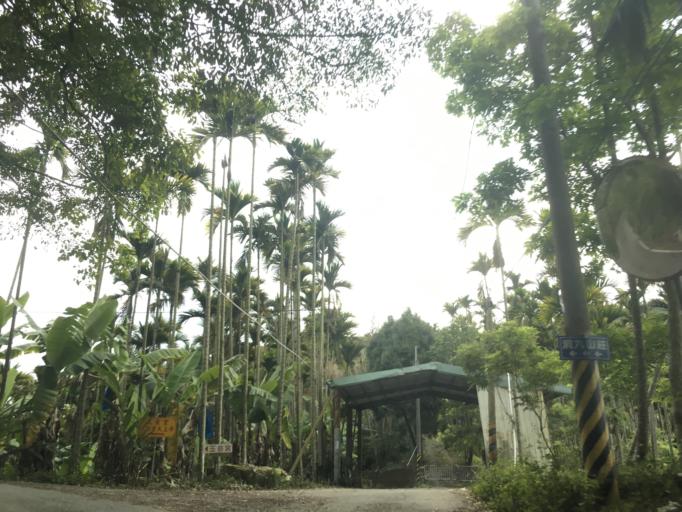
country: TW
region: Taiwan
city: Zhongxing New Village
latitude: 23.9700
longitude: 120.8166
